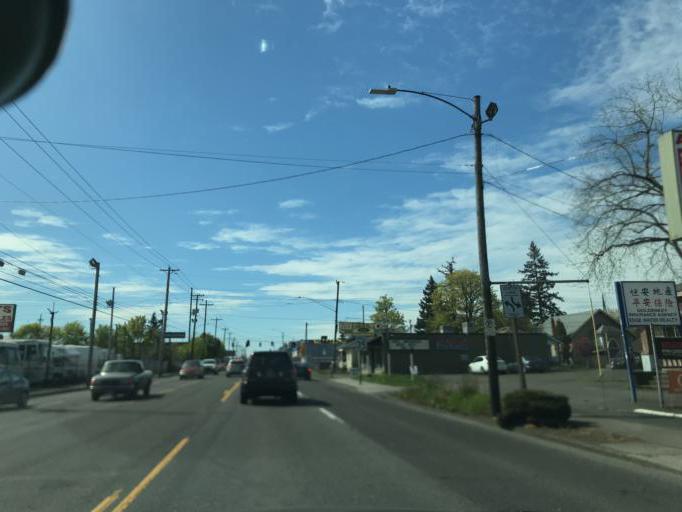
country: US
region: Oregon
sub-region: Multnomah County
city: Lents
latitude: 45.4809
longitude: -122.5790
